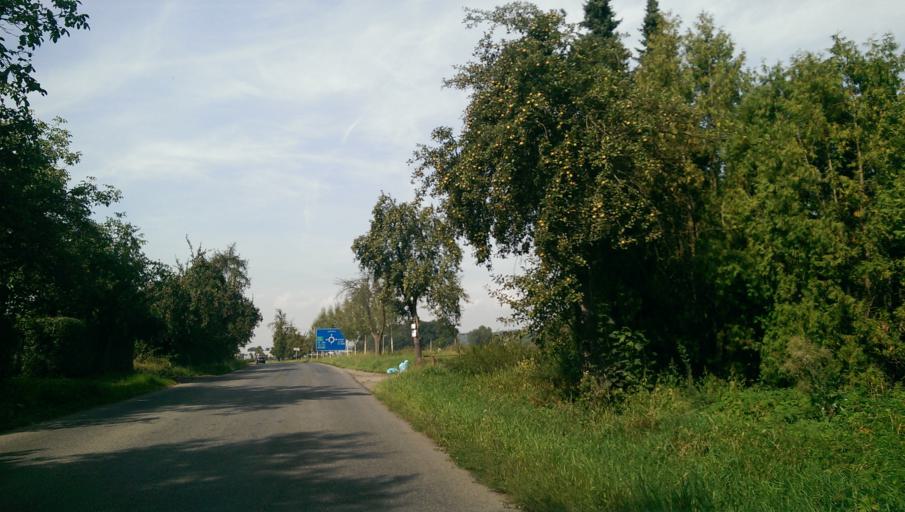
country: CZ
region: Liberecky
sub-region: Okres Semily
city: Turnov
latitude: 50.6011
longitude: 15.1541
